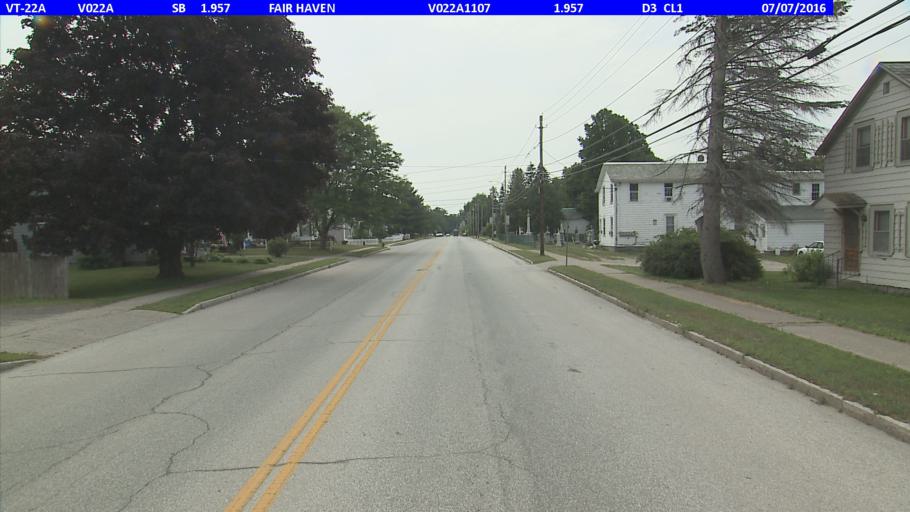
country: US
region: Vermont
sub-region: Rutland County
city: Fair Haven
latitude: 43.5990
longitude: -73.2715
